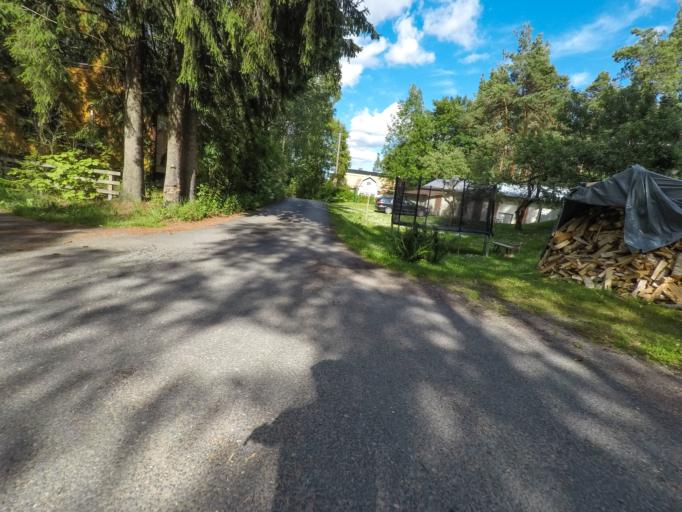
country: FI
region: South Karelia
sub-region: Lappeenranta
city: Joutseno
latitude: 61.1252
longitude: 28.4903
